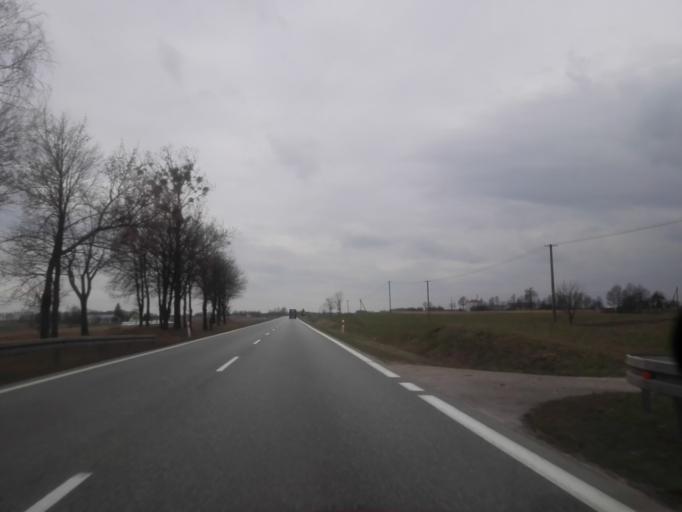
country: PL
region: Podlasie
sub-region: Powiat augustowski
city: Augustow
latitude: 53.8146
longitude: 22.9201
